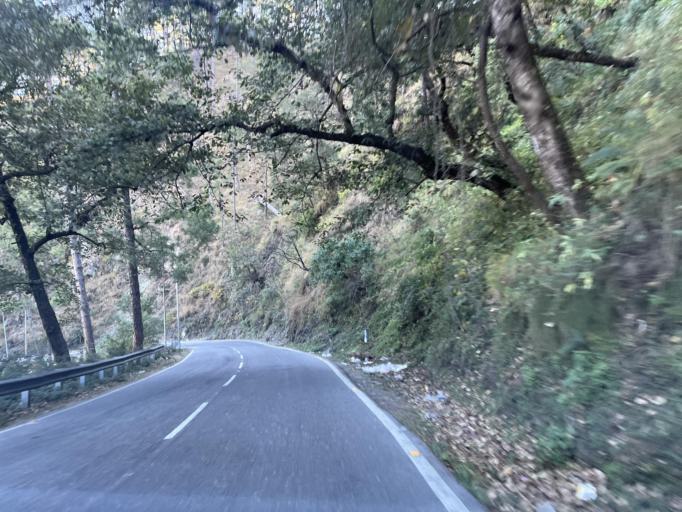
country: IN
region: Uttarakhand
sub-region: Naini Tal
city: Bhowali
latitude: 29.4020
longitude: 79.5103
